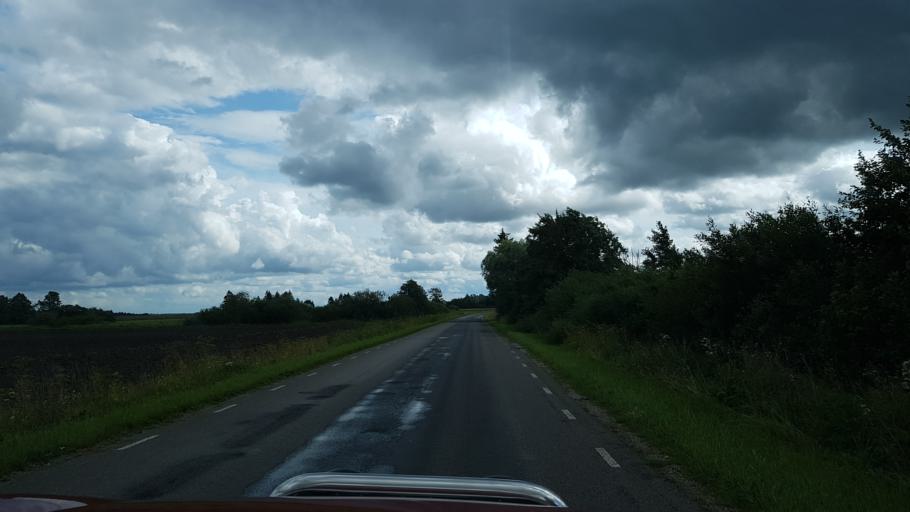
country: EE
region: Laeaene
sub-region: Lihula vald
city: Lihula
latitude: 58.7166
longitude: 23.9916
